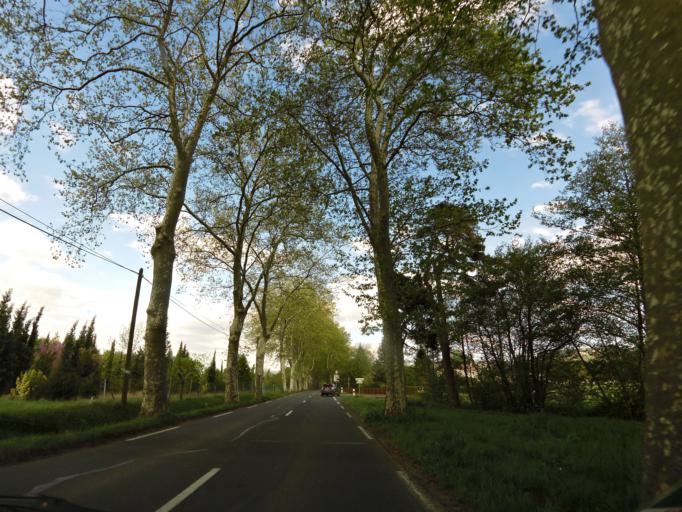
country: FR
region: Midi-Pyrenees
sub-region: Departement de la Haute-Garonne
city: Revel
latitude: 43.4533
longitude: 2.0239
